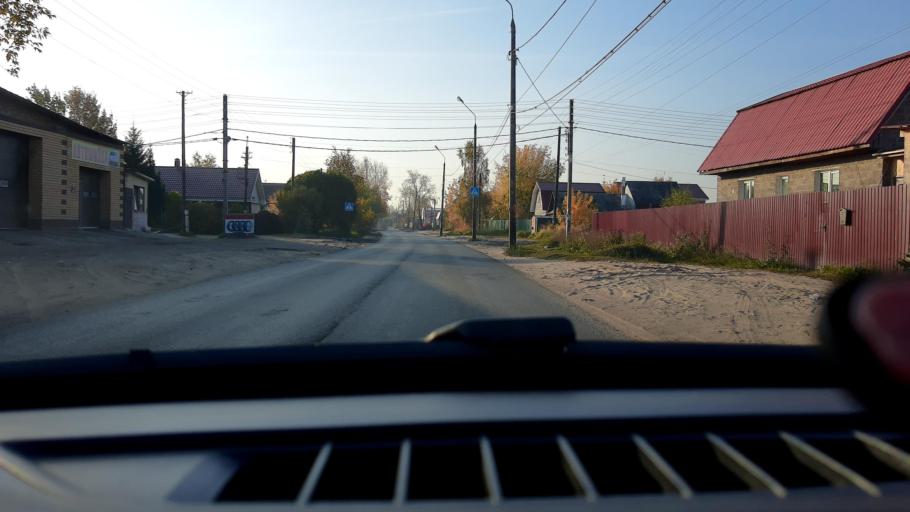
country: RU
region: Nizjnij Novgorod
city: Gorbatovka
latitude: 56.3013
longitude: 43.8461
